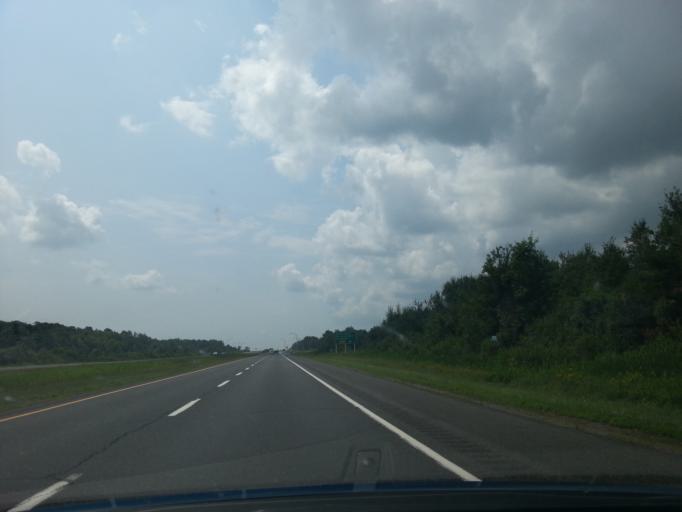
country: CA
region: Quebec
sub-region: Chaudiere-Appalaches
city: Saint-Antoine-de-Tilly
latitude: 46.5827
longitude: -71.5584
